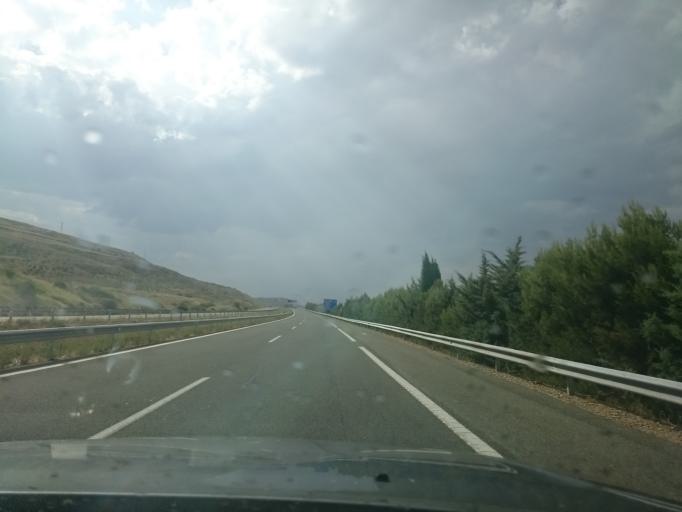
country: ES
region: La Rioja
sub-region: Provincia de La Rioja
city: Arrubal
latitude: 42.4253
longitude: -2.2700
